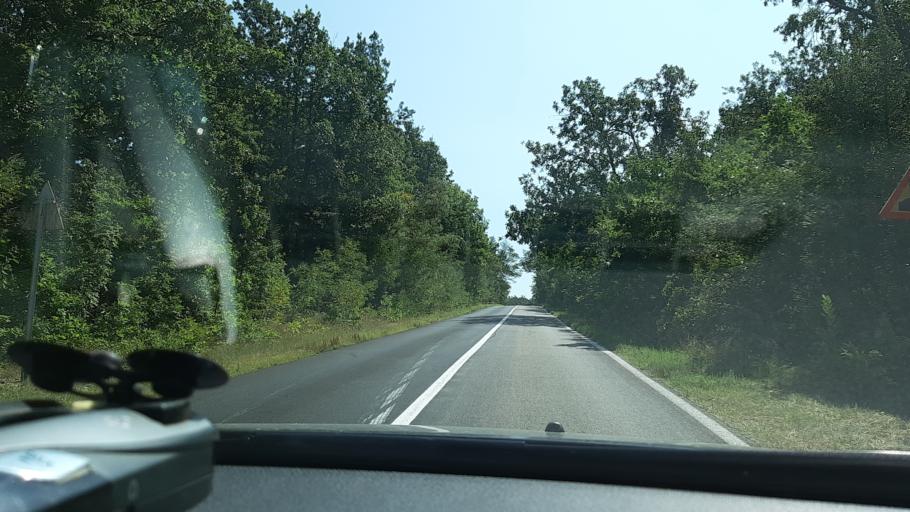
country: RO
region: Gorj
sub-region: Comuna Licuriciu
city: Licuriciu
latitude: 44.9462
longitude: 23.5718
